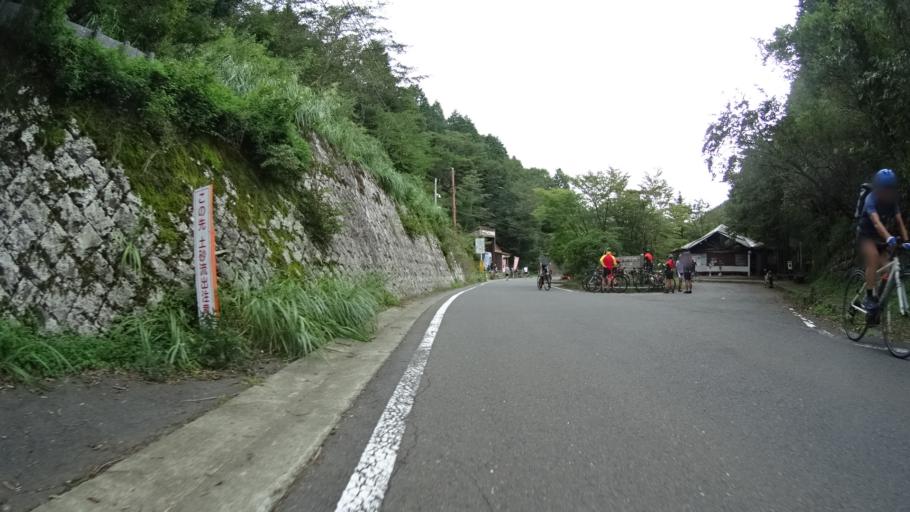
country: JP
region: Kanagawa
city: Hadano
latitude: 35.4277
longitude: 139.2196
